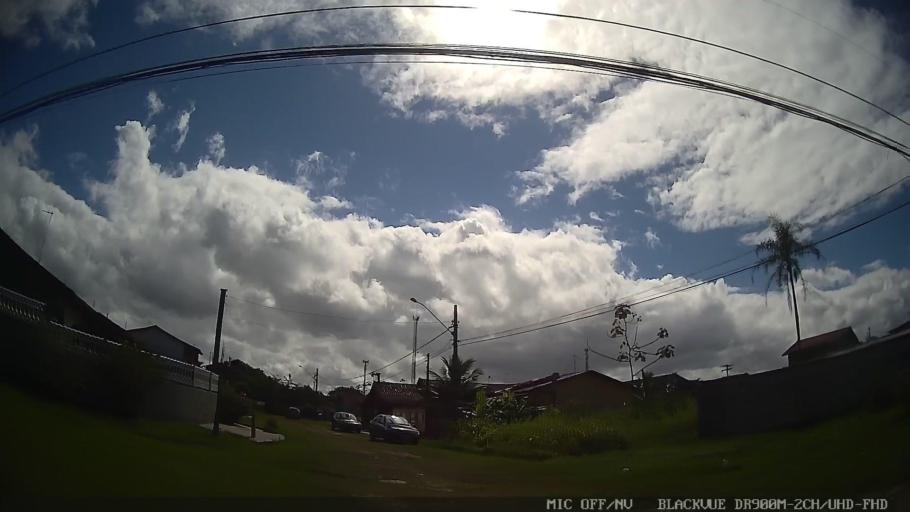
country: BR
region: Sao Paulo
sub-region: Itanhaem
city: Itanhaem
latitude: -24.2266
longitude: -46.8760
